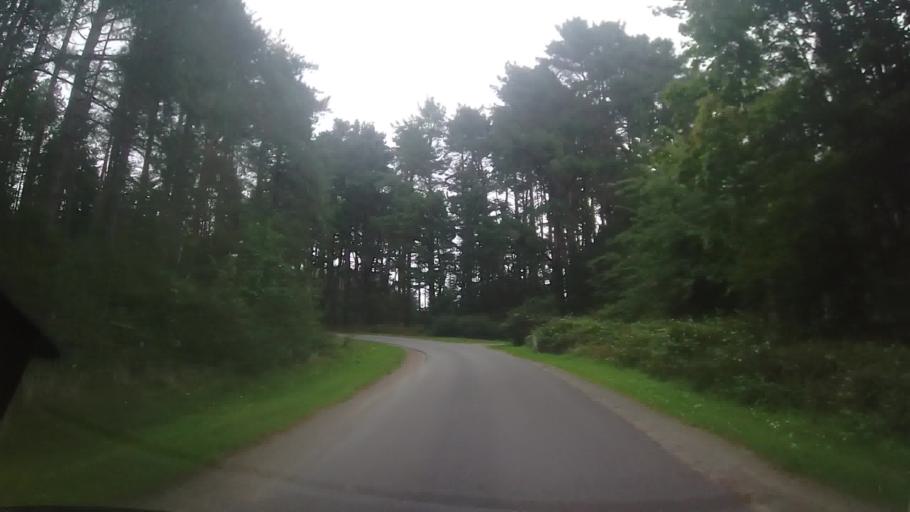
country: GB
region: Wales
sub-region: Gwynedd
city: Caernarfon
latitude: 53.1540
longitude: -4.3746
